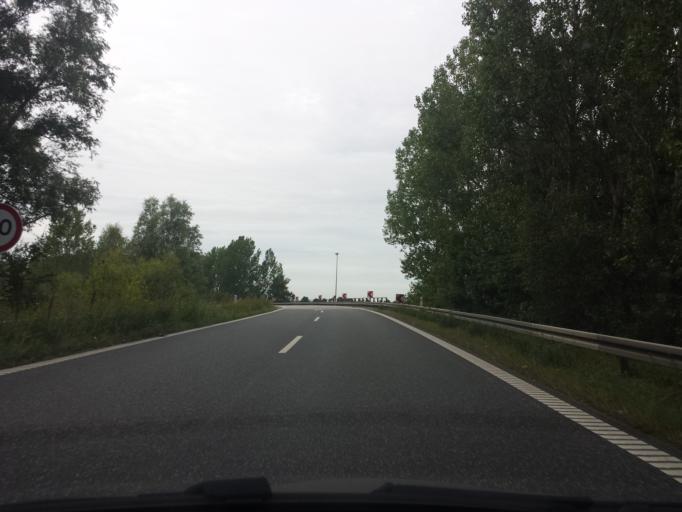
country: DK
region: Capital Region
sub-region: Hoje-Taastrup Kommune
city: Flong
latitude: 55.6542
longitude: 12.2091
